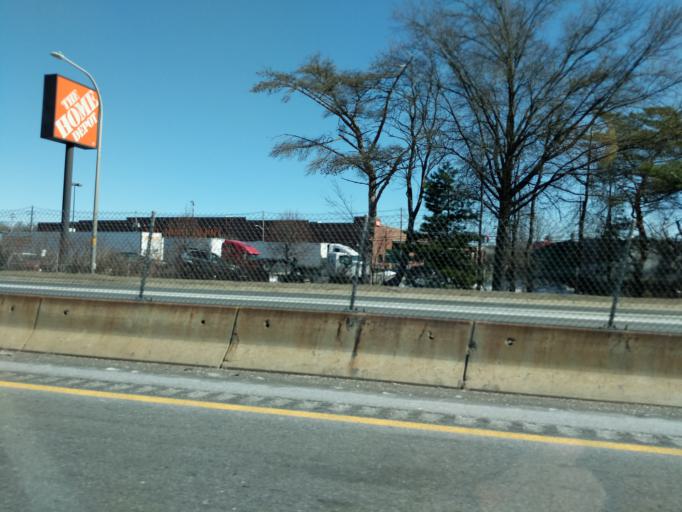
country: US
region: Rhode Island
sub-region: Providence County
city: Providence
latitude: 41.8428
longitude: -71.4192
